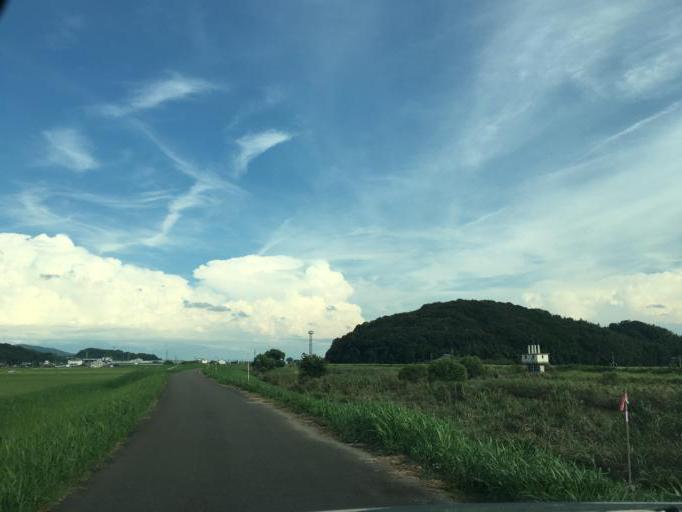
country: JP
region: Saga Prefecture
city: Takeocho-takeo
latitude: 33.2135
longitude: 130.0770
